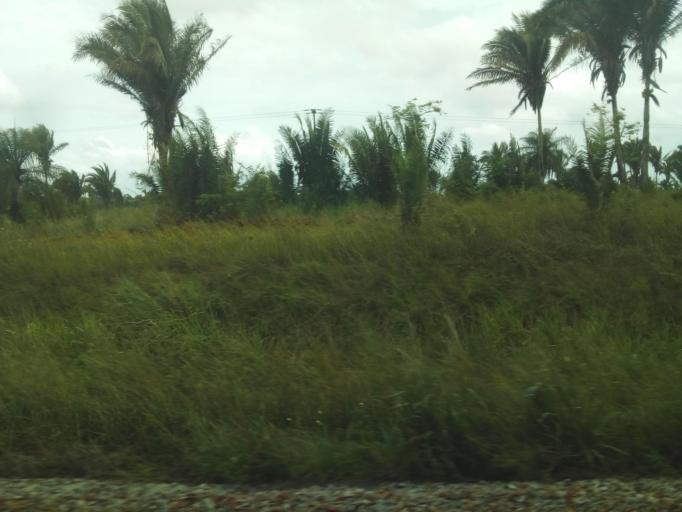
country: BR
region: Maranhao
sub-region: Arari
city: Arari
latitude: -3.5737
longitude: -44.7258
